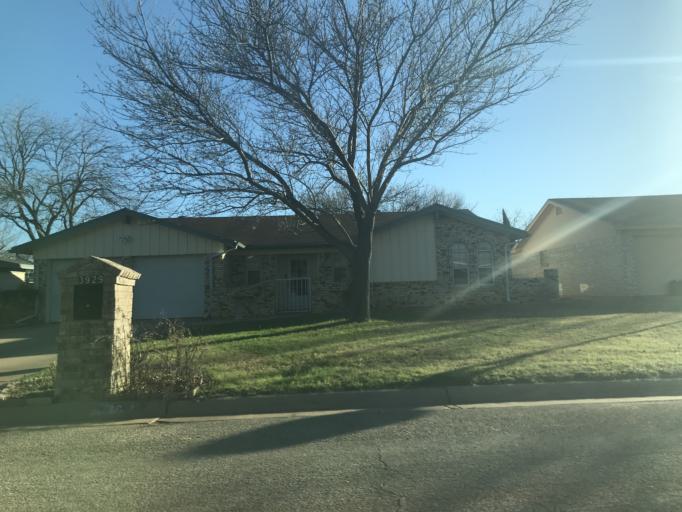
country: US
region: Texas
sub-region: Tom Green County
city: San Angelo
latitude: 31.4313
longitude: -100.4943
